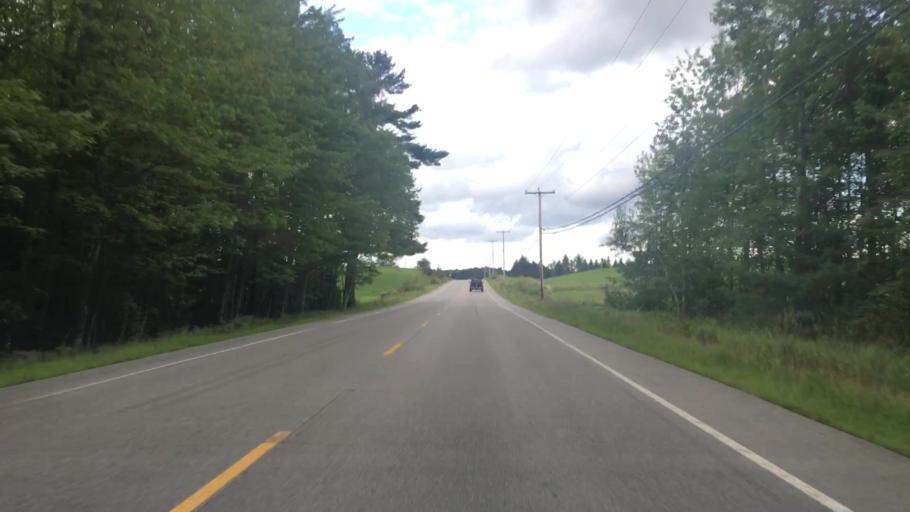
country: US
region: Maine
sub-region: York County
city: Dayton
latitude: 43.5412
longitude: -70.5633
